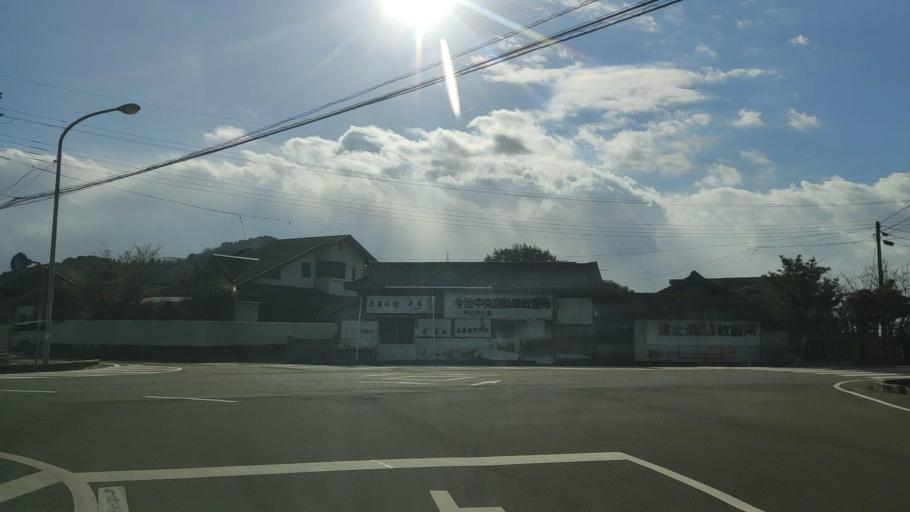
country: JP
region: Hiroshima
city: Innoshima
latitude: 34.2213
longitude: 133.0673
